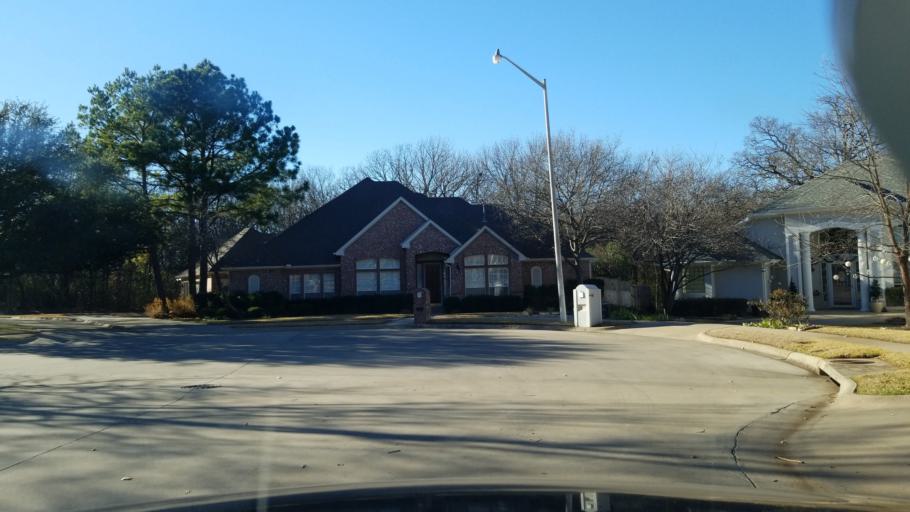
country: US
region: Texas
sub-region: Denton County
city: Corinth
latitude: 33.1487
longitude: -97.1213
